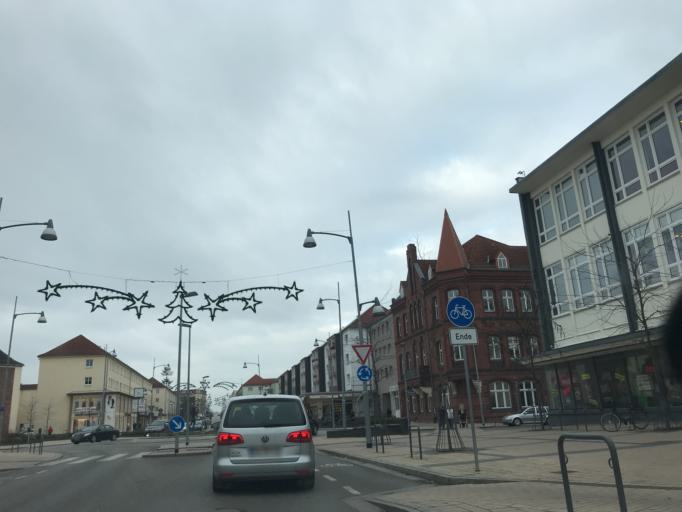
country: DE
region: Brandenburg
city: Rathenow
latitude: 52.6058
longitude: 12.3410
